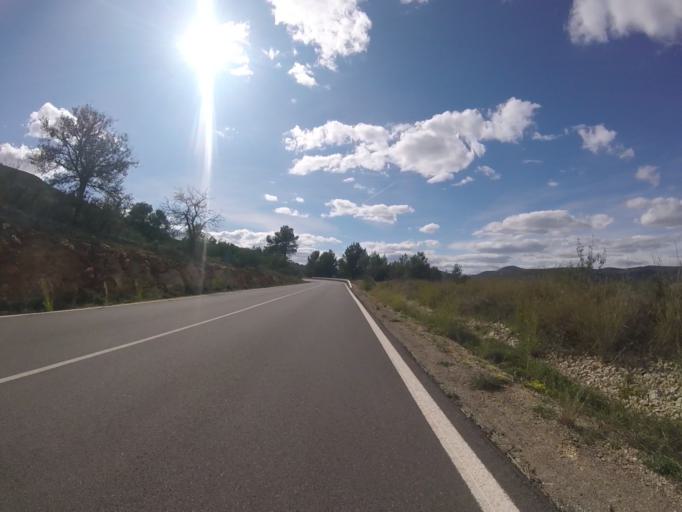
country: ES
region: Valencia
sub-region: Provincia de Castello
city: Cati
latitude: 40.4352
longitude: 0.0971
